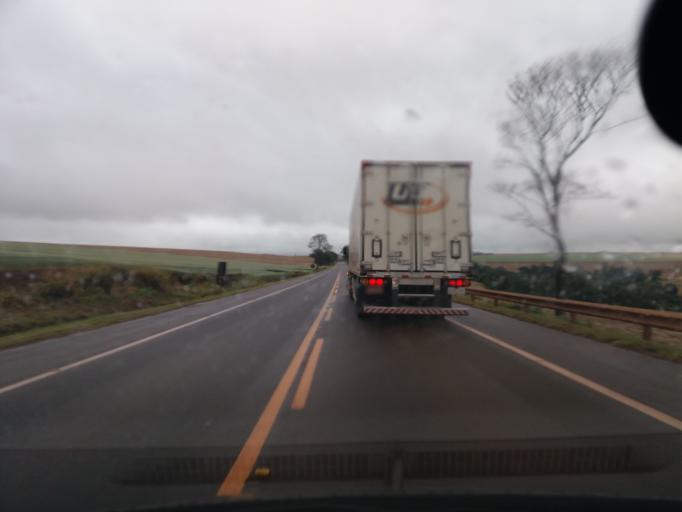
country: BR
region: Parana
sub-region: Campo Mourao
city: Campo Mourao
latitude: -24.3305
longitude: -52.6565
